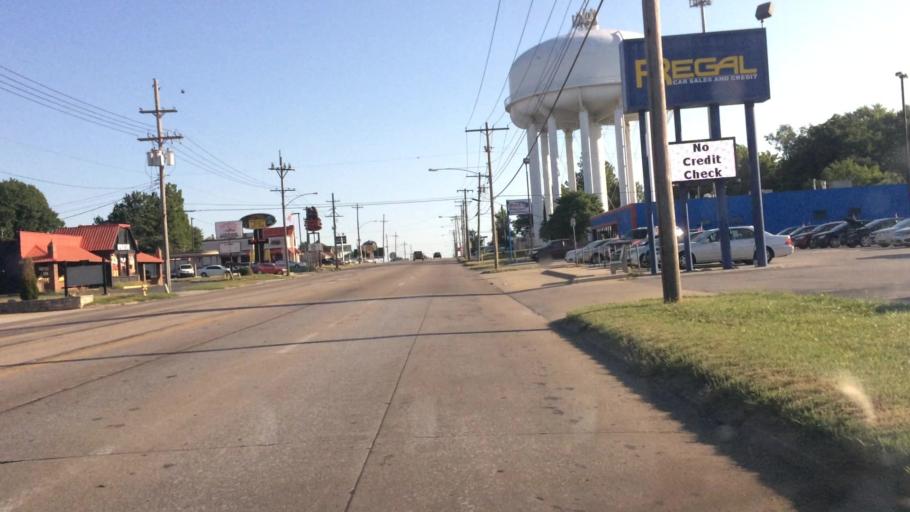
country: US
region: Missouri
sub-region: Greene County
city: Springfield
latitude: 37.1995
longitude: -93.2620
